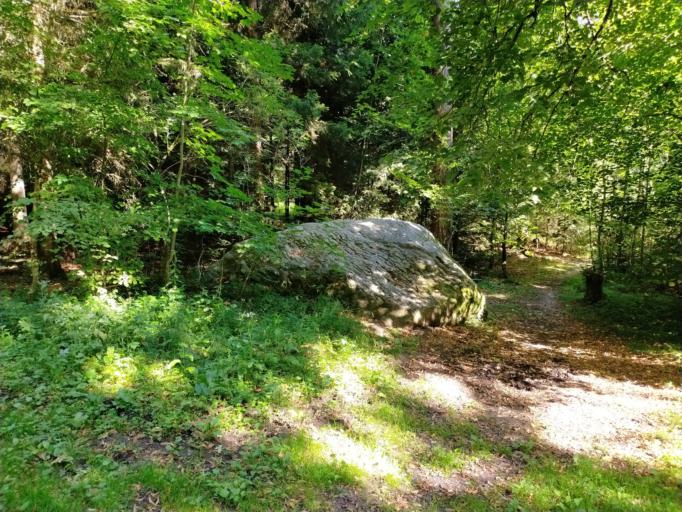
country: CH
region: Vaud
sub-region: Lavaux-Oron District
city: Oron-la-ville
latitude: 46.5707
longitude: 6.8466
